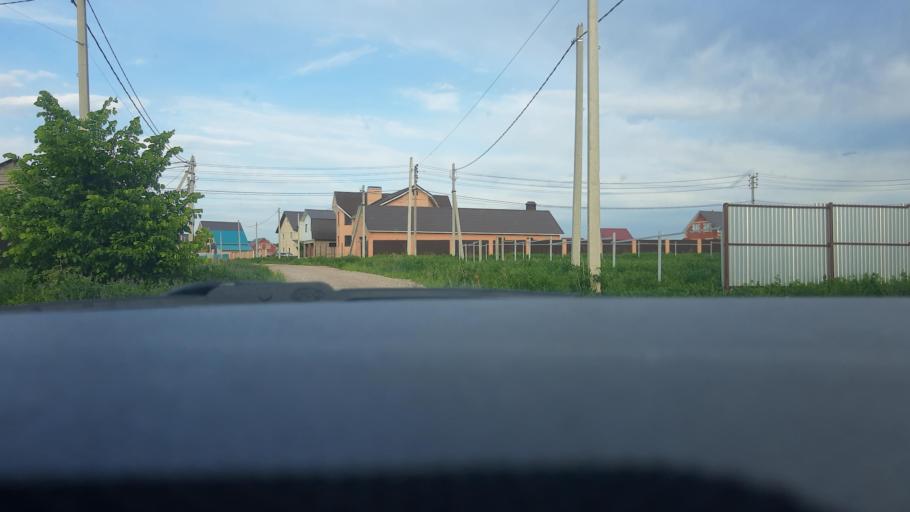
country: RU
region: Bashkortostan
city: Kabakovo
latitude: 54.6056
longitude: 56.1216
